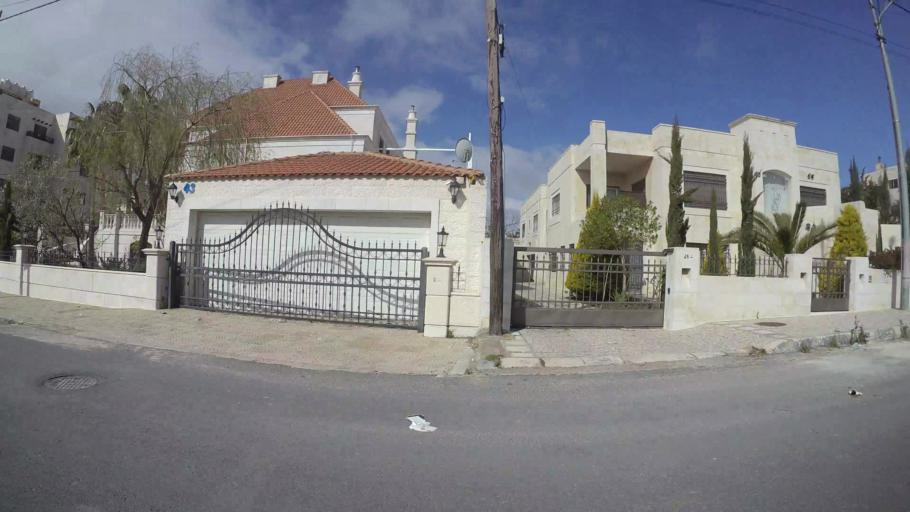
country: JO
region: Amman
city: Al Jubayhah
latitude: 32.0037
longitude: 35.8437
